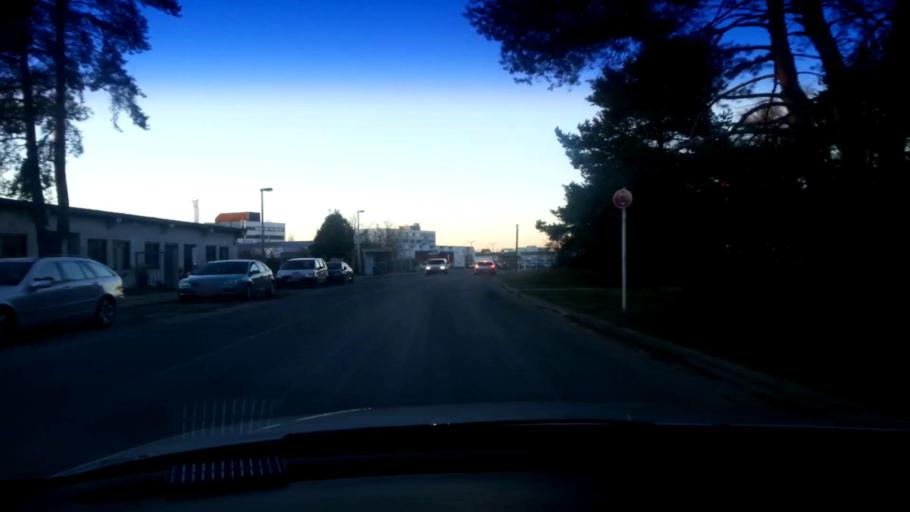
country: DE
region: Bavaria
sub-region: Upper Franconia
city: Bamberg
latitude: 49.8827
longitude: 10.9250
